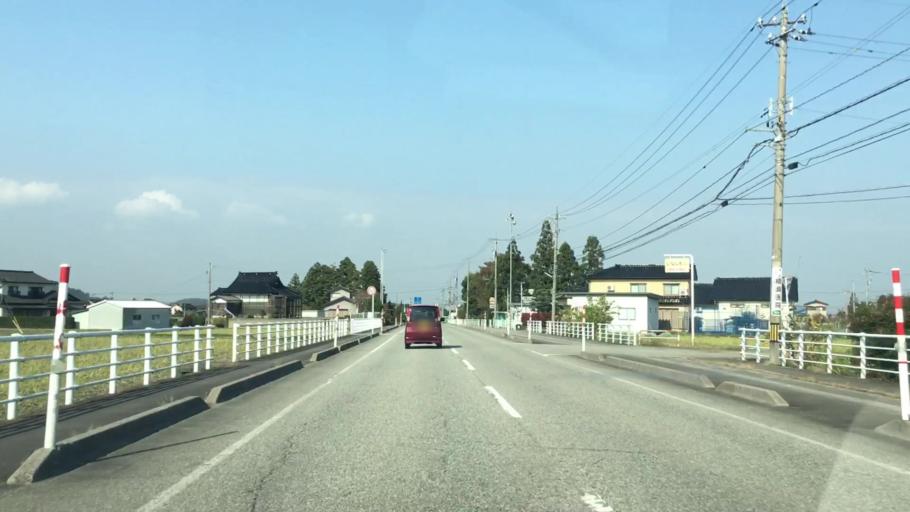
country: JP
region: Toyama
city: Yatsuomachi-higashikumisaka
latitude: 36.5727
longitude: 137.1954
